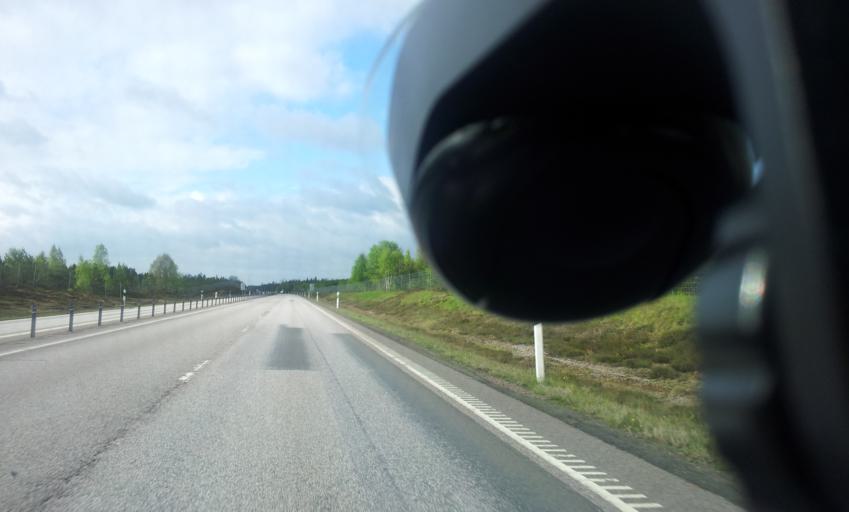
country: SE
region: Kalmar
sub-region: Torsas Kommun
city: Torsas
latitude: 56.4869
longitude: 16.0835
